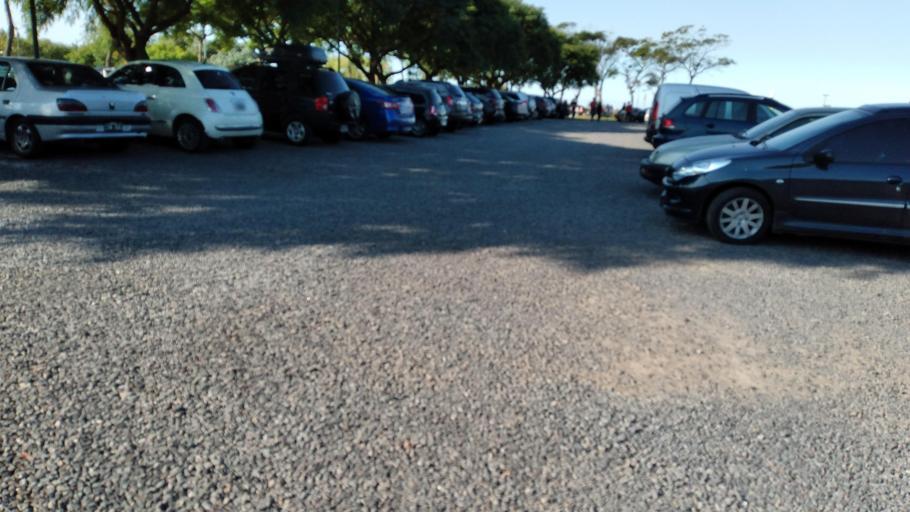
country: AR
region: Buenos Aires
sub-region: Partido de Vicente Lopez
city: Olivos
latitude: -34.5003
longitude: -58.4787
